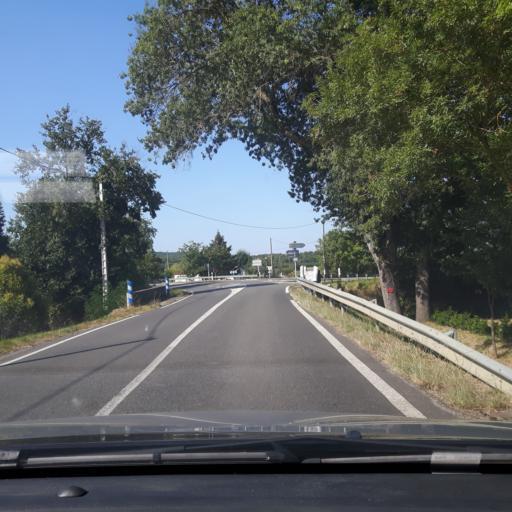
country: FR
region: Midi-Pyrenees
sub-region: Departement de la Haute-Garonne
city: Paulhac
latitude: 43.7820
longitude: 1.5575
